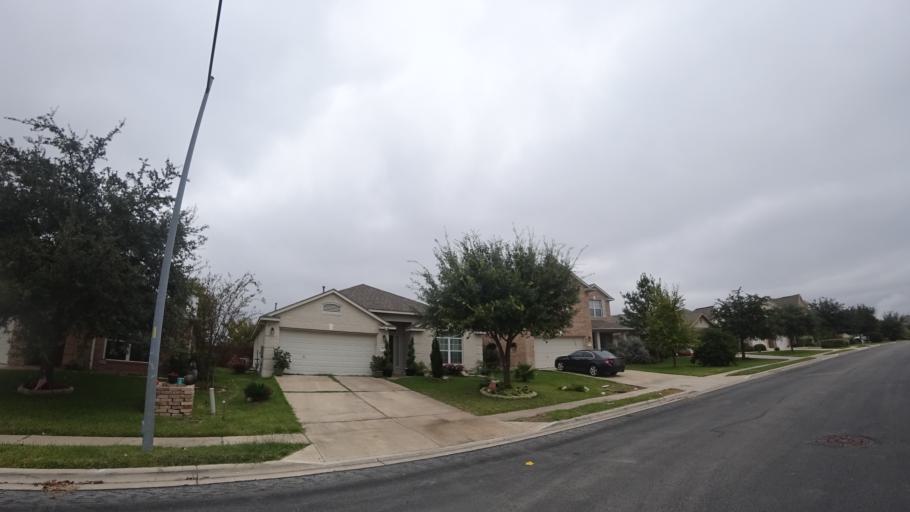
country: US
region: Texas
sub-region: Travis County
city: Pflugerville
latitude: 30.3756
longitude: -97.6487
